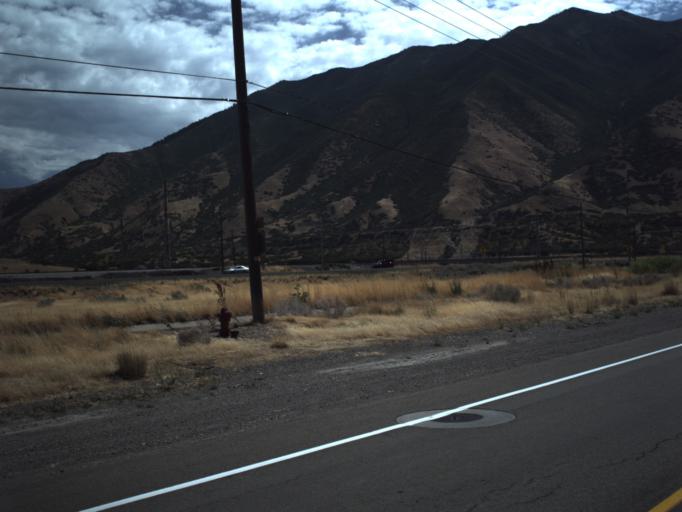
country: US
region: Utah
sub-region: Utah County
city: Mapleton
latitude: 40.0911
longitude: -111.5996
